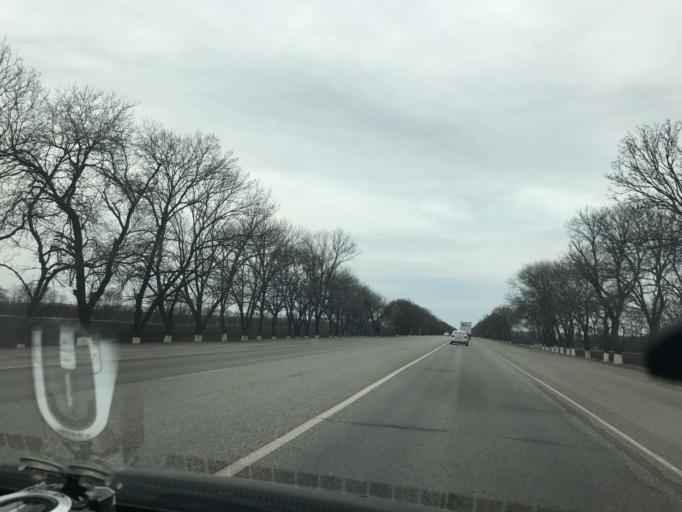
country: RU
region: Krasnodarskiy
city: Zavetnyy
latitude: 44.9367
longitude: 41.1091
